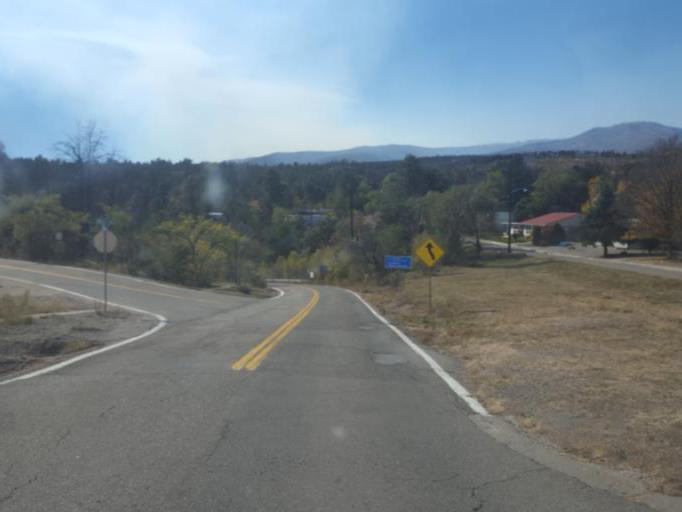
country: US
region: New Mexico
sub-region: Los Alamos County
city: Los Alamos
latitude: 35.8822
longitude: -106.3210
